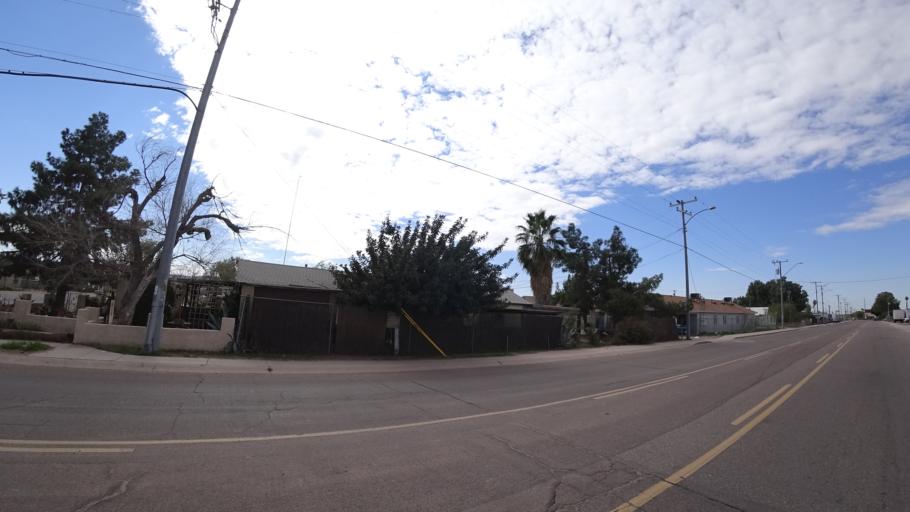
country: US
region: Arizona
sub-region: Maricopa County
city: Phoenix
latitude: 33.4314
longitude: -112.0697
